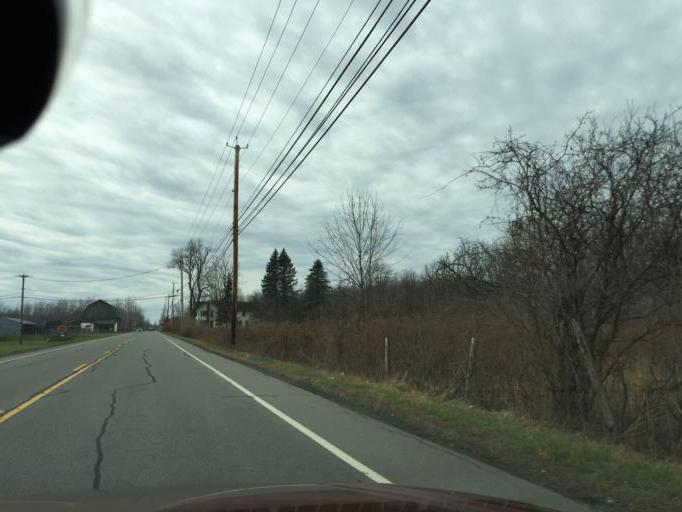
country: US
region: New York
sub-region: Monroe County
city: Scottsville
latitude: 43.0931
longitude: -77.7035
